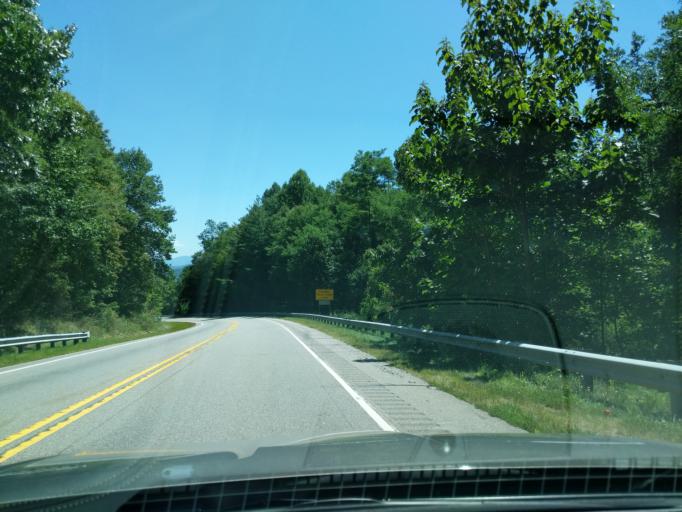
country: US
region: North Carolina
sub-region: Macon County
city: Franklin
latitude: 35.1302
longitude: -83.5326
